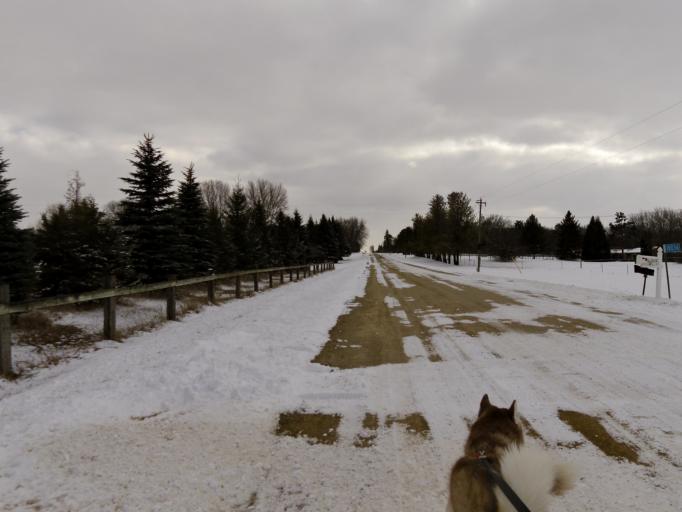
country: US
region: Minnesota
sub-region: Scott County
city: Prior Lake
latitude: 44.6882
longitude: -93.4526
